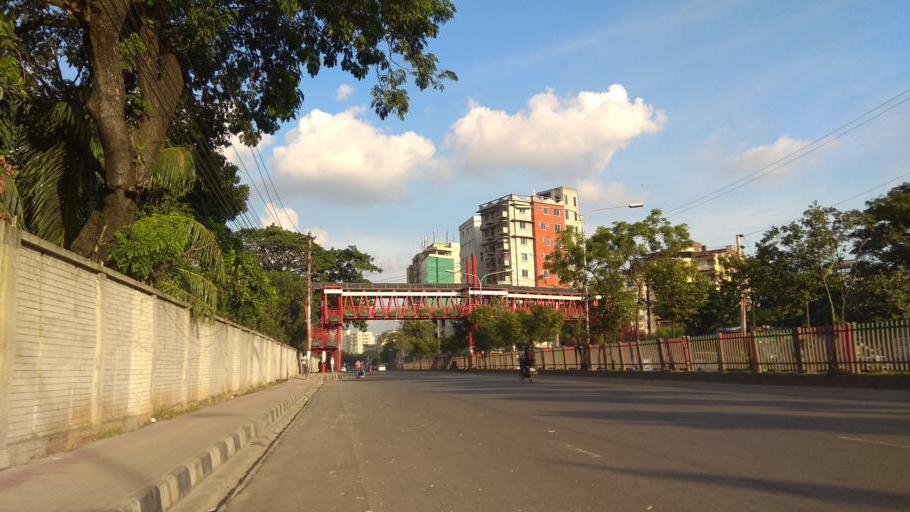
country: BD
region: Dhaka
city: Azimpur
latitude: 23.7807
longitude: 90.3536
